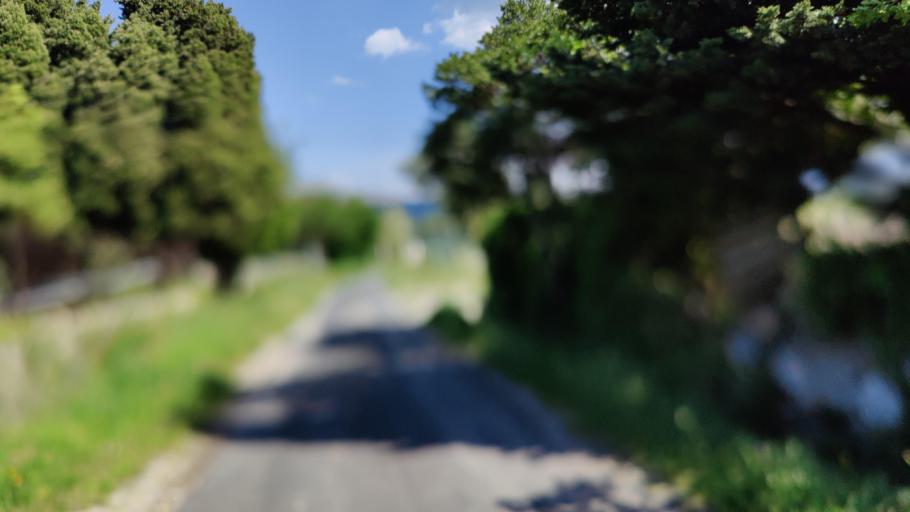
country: FR
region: Languedoc-Roussillon
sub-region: Departement des Pyrenees-Orientales
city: Estagel
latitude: 42.8863
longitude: 2.7184
